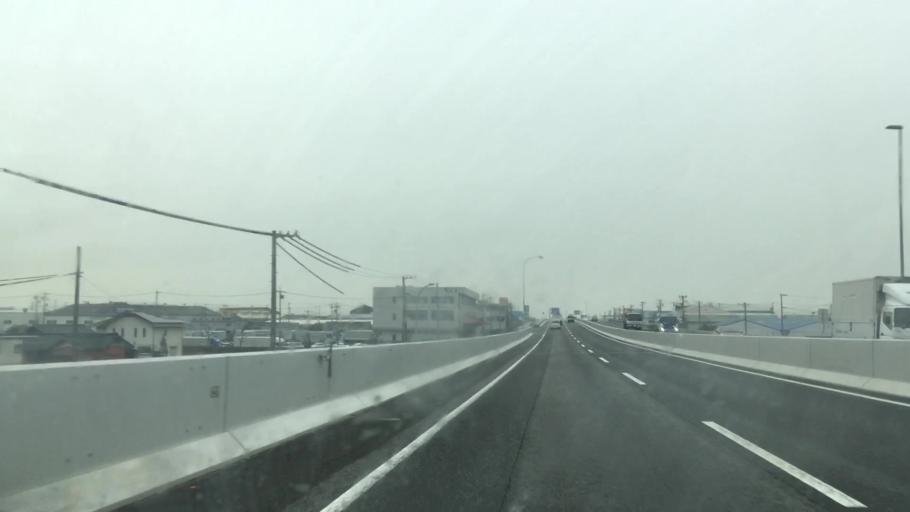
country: JP
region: Aichi
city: Anjo
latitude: 34.9195
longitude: 137.0556
